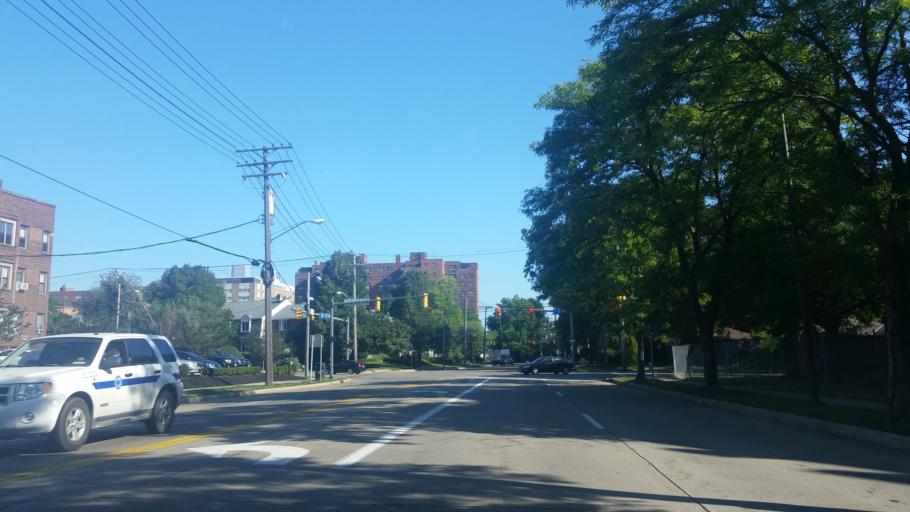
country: US
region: Ohio
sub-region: Cuyahoga County
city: Lakewood
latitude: 41.4882
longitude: -81.7687
